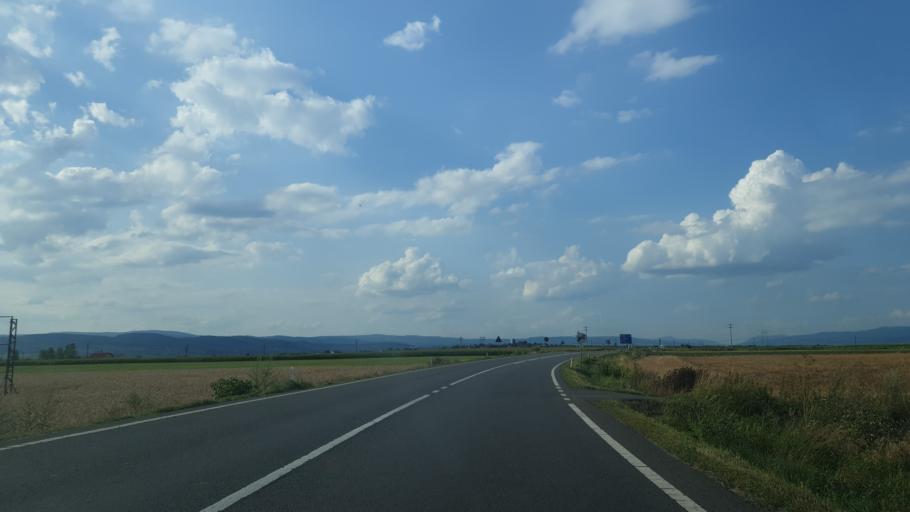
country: RO
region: Covasna
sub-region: Comuna Chichis
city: Chichis
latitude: 45.7946
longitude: 25.8045
